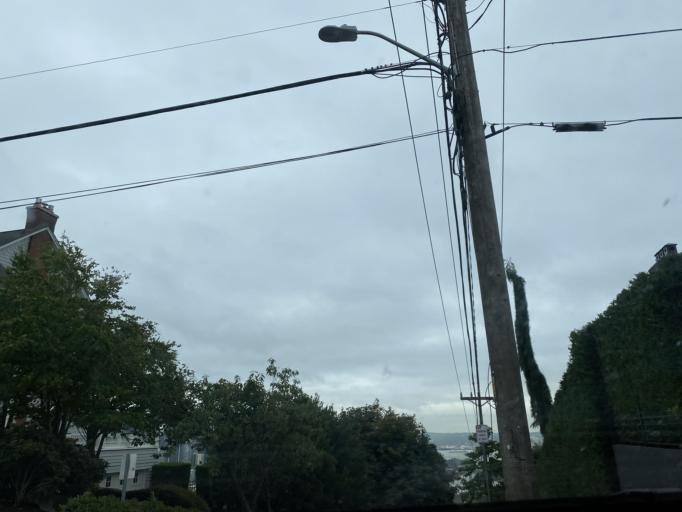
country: US
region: Washington
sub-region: King County
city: Seattle
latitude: 47.6298
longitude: -122.3541
